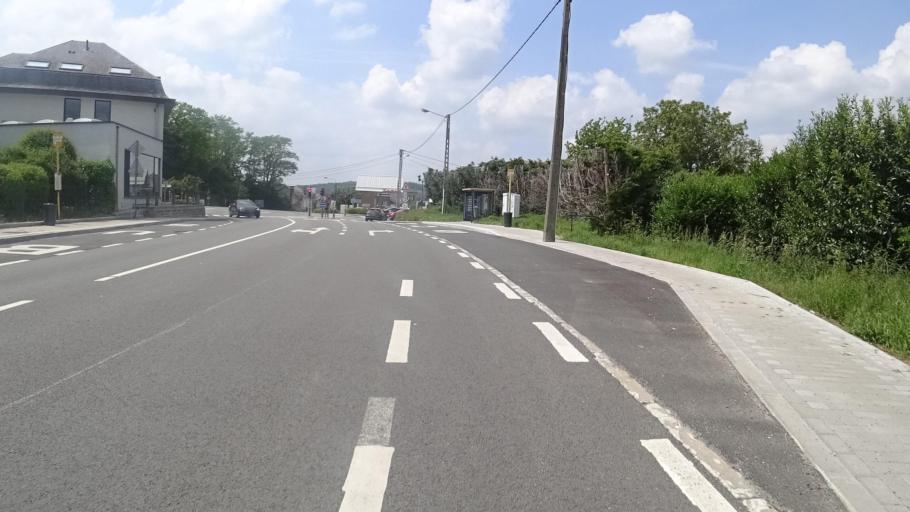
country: BE
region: Wallonia
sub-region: Province du Brabant Wallon
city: Wavre
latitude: 50.7101
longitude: 4.6174
